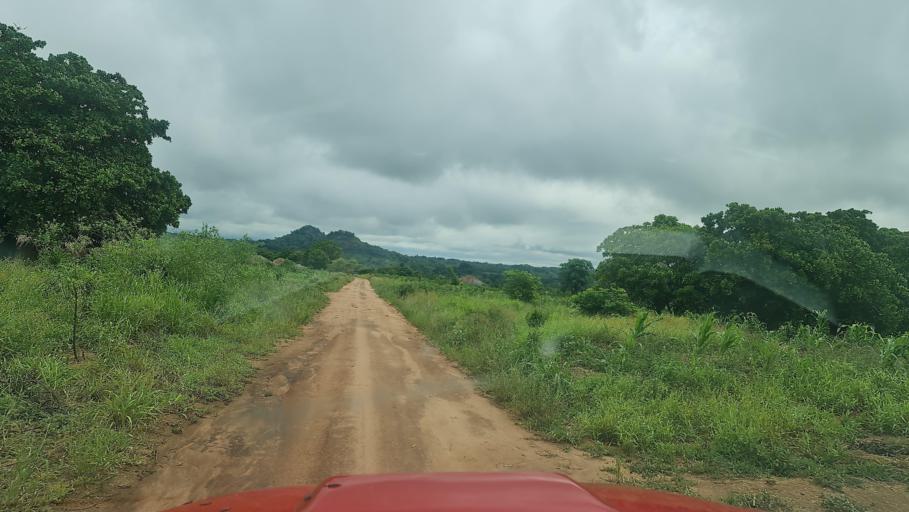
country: MW
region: Southern Region
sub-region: Nsanje District
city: Nsanje
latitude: -17.1831
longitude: 35.9278
